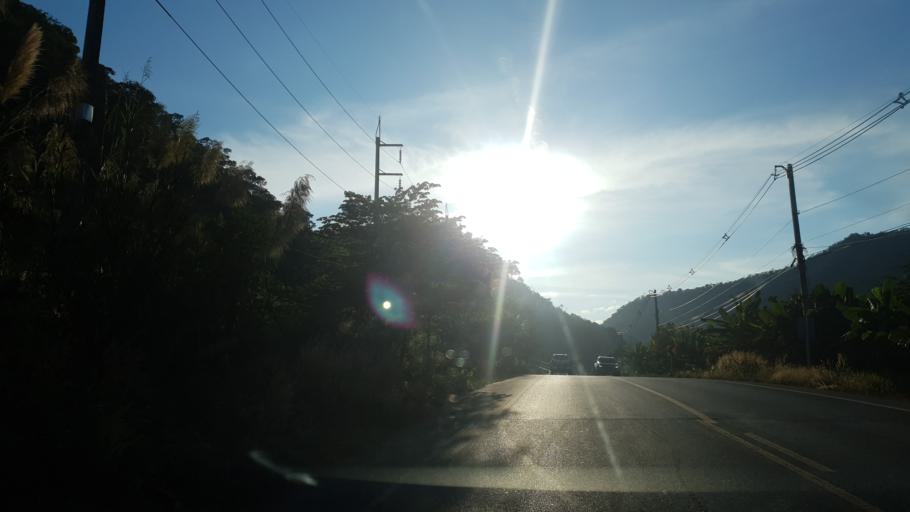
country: TH
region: Loei
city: Dan Sai
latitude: 17.2269
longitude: 101.0371
